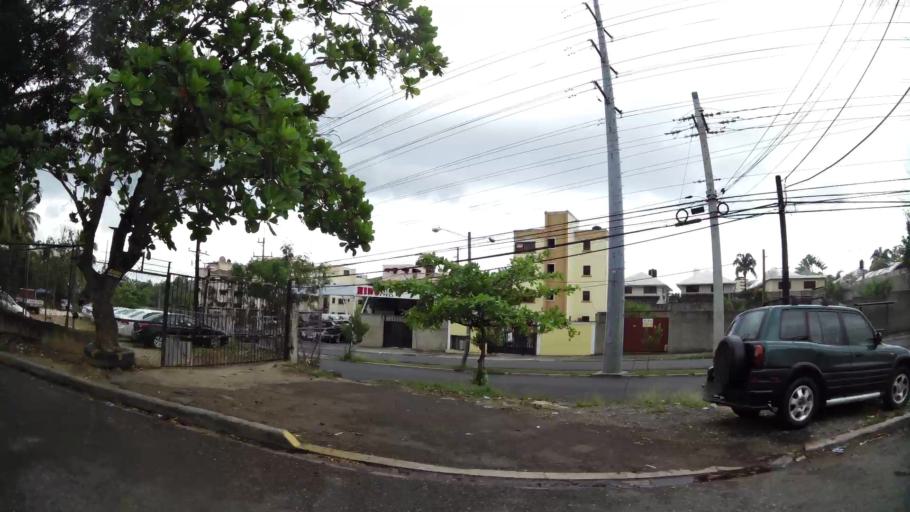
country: DO
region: Nacional
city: La Agustina
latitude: 18.5021
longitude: -69.9409
